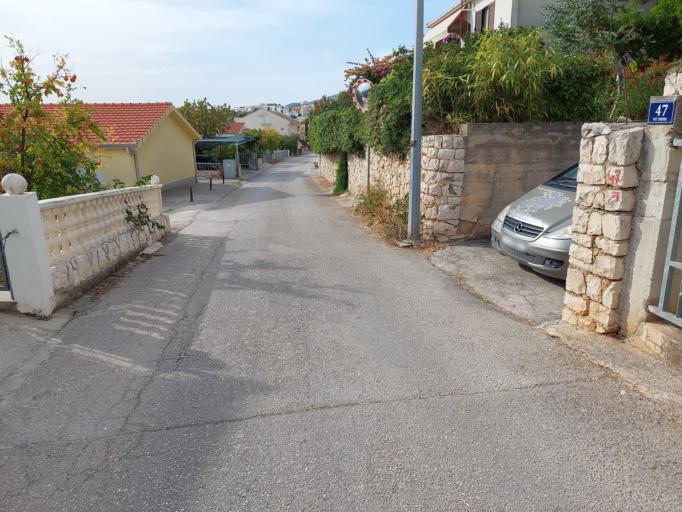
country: HR
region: Splitsko-Dalmatinska
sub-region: Grad Trogir
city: Trogir
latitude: 43.4912
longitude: 16.2786
